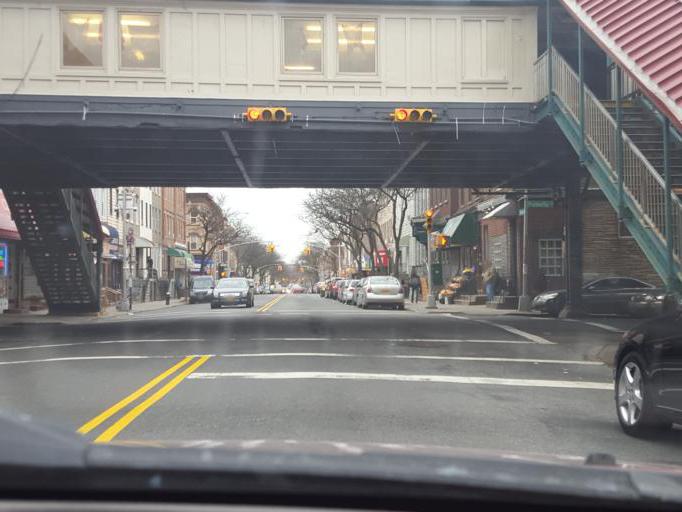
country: US
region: New York
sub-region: Kings County
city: East New York
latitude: 40.7030
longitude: -73.9080
